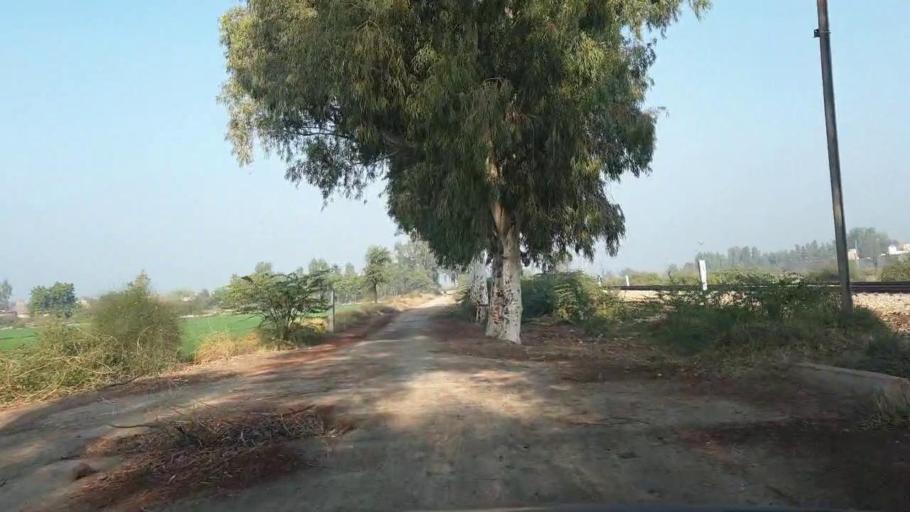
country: PK
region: Sindh
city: Shahdadpur
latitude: 25.9696
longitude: 68.6069
